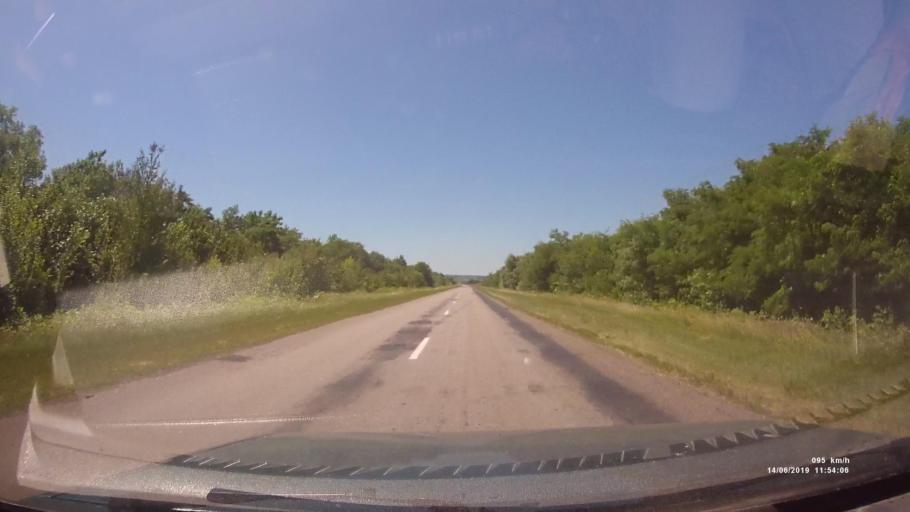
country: RU
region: Rostov
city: Kazanskaya
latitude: 49.8218
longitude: 41.2005
